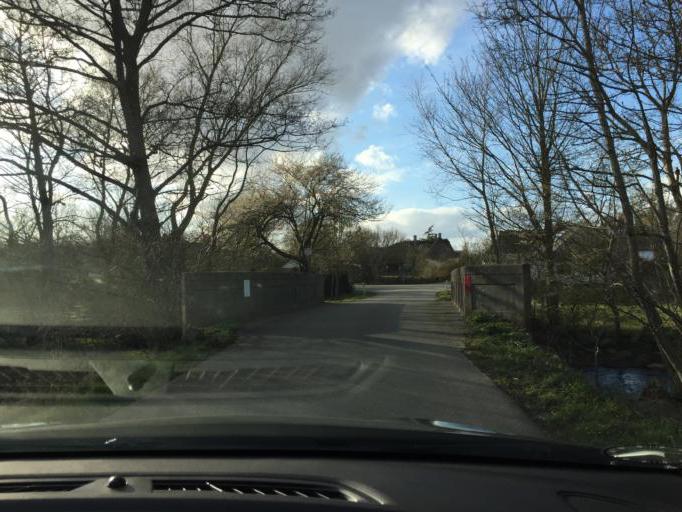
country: DK
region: South Denmark
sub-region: Kerteminde Kommune
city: Langeskov
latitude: 55.3430
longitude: 10.6089
